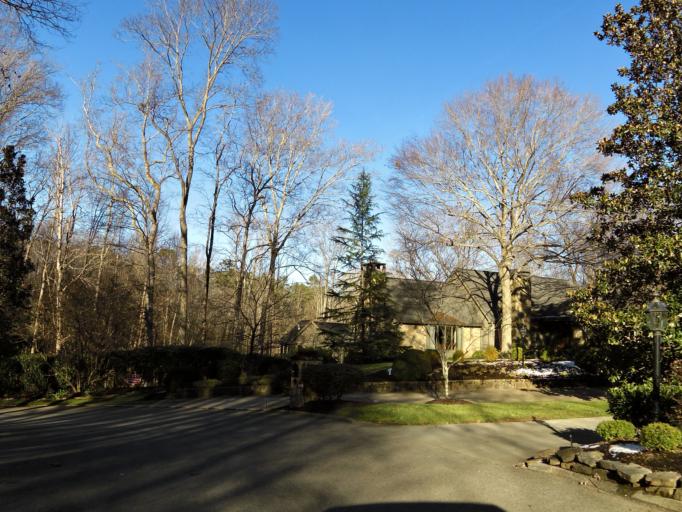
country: US
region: Tennessee
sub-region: Knox County
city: Knoxville
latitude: 35.8918
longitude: -83.9693
